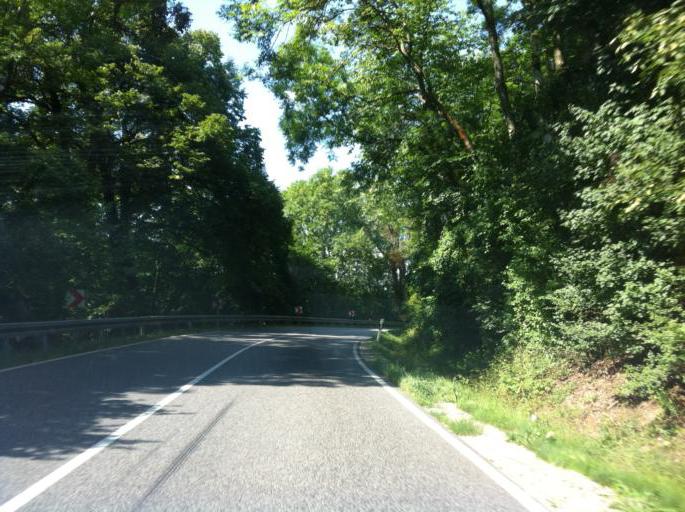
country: DE
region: Thuringia
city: Heilbad Heiligenstadt
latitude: 51.3640
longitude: 10.1675
